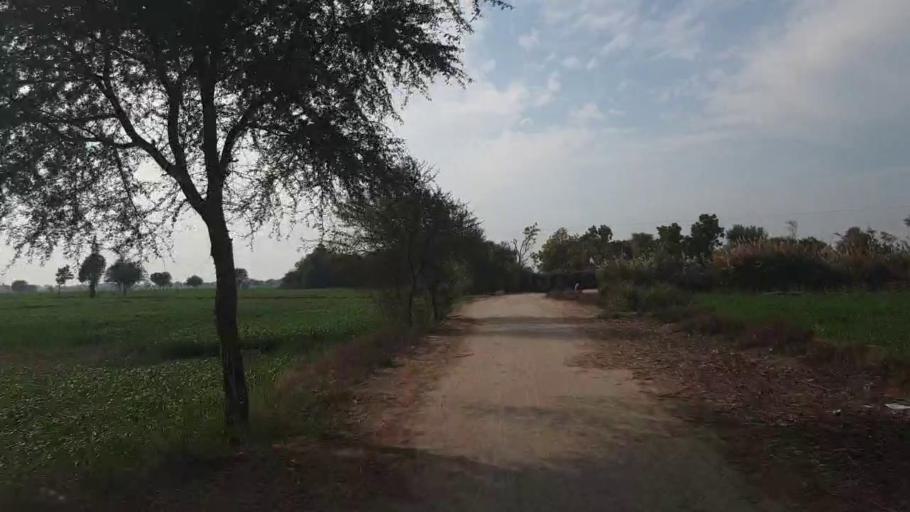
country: PK
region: Sindh
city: Shahdadpur
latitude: 26.0159
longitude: 68.5208
